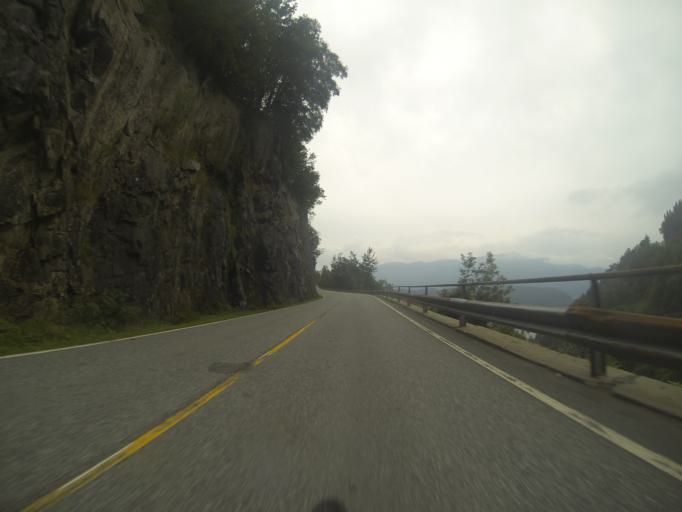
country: NO
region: Rogaland
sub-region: Suldal
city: Sand
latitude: 59.5385
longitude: 6.2567
